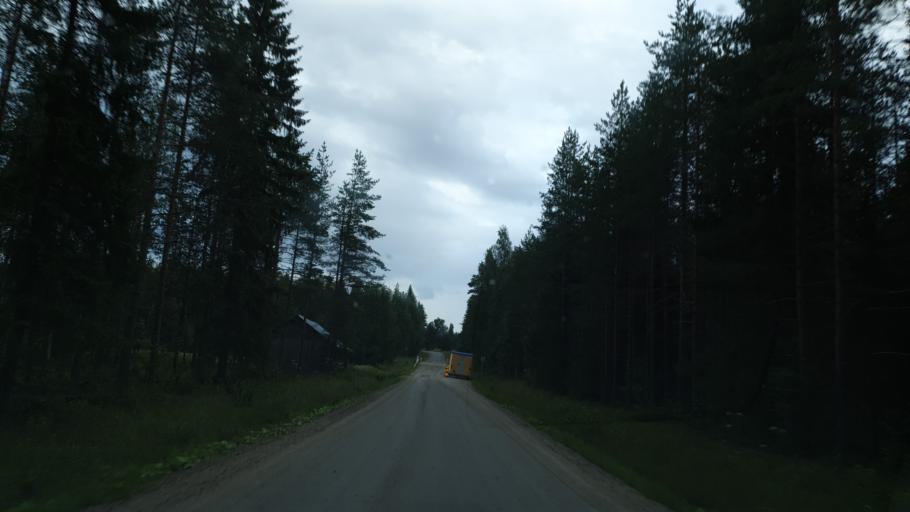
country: FI
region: Kainuu
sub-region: Kehys-Kainuu
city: Kuhmo
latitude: 64.2092
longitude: 29.3704
